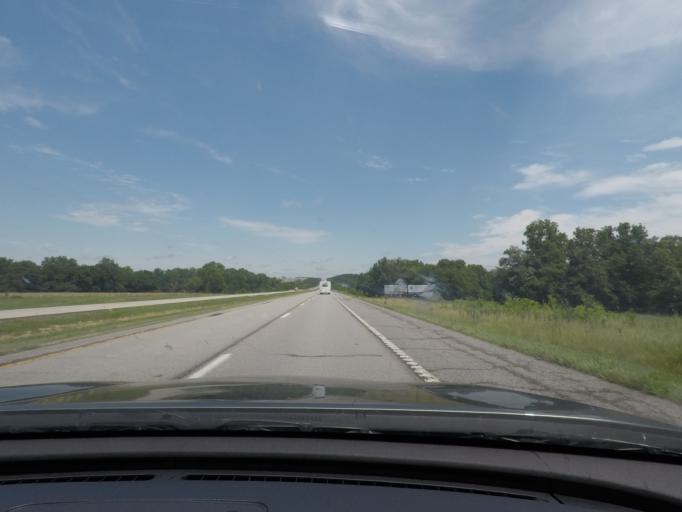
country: US
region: Missouri
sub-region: Saline County
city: Marshall
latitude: 38.9889
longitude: -93.1966
